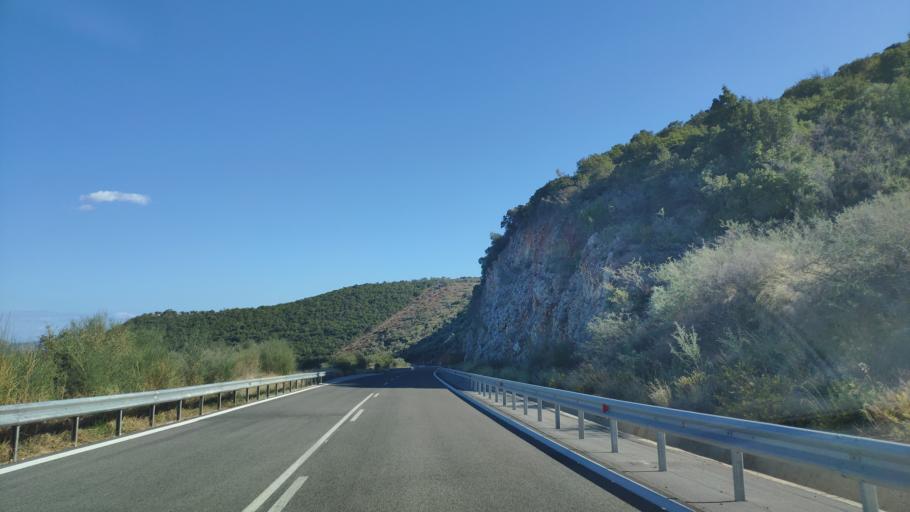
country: GR
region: Peloponnese
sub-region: Nomos Argolidos
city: Didyma
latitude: 37.5549
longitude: 23.2626
